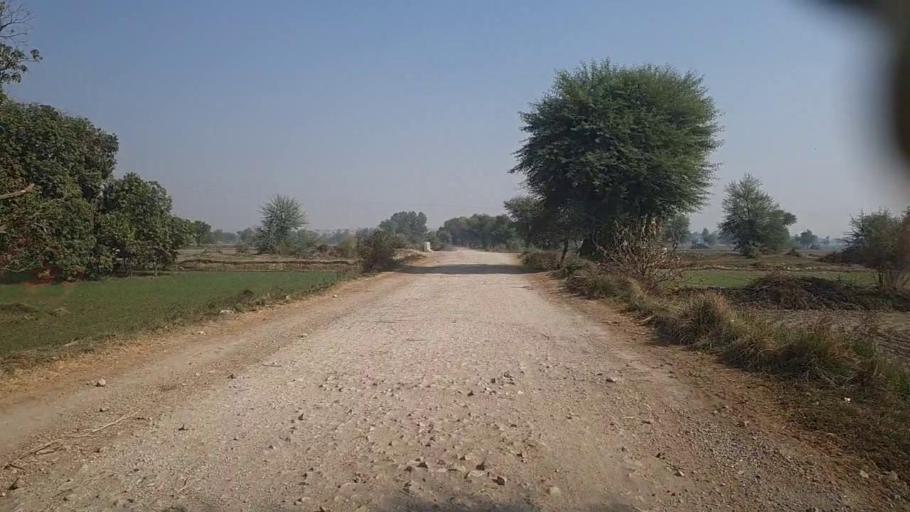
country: PK
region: Sindh
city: Kandiari
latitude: 26.9272
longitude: 68.5218
